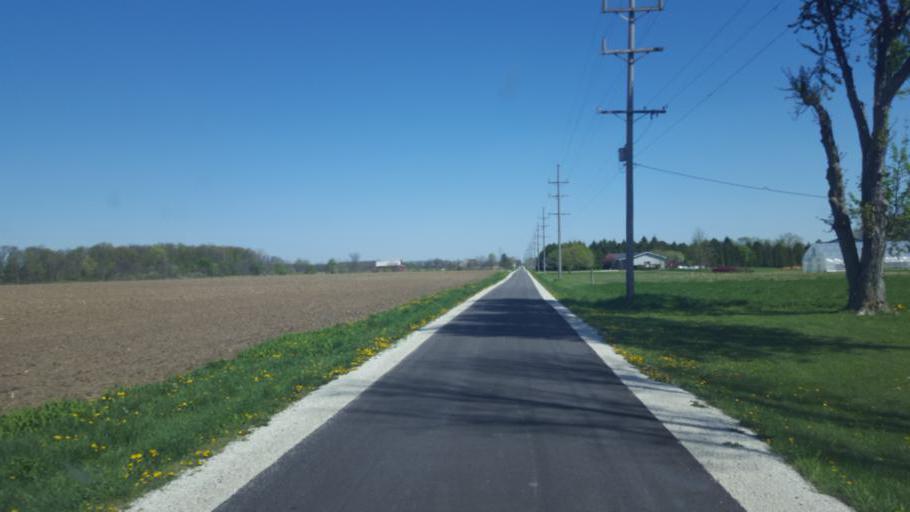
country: US
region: Ohio
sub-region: Sandusky County
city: Ballville
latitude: 41.2550
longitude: -83.1877
